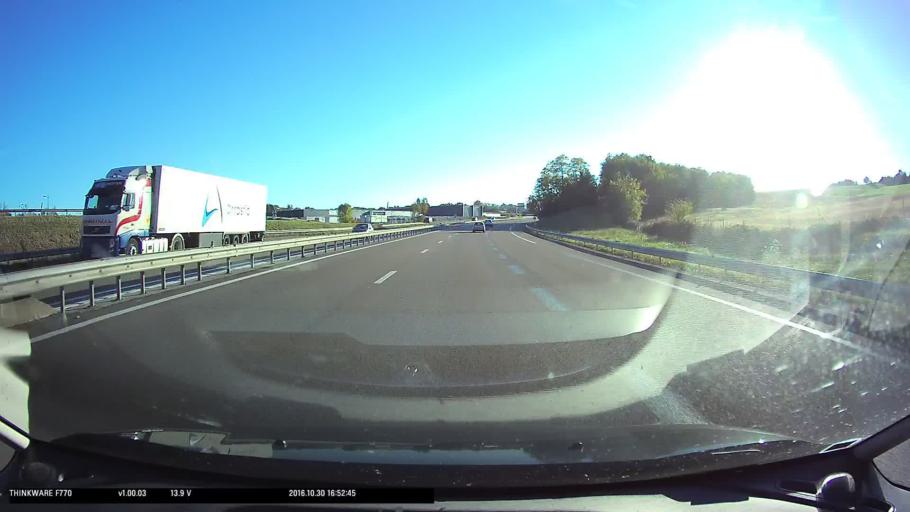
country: FR
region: Franche-Comte
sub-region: Departement du Doubs
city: Chemaudin
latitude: 47.2356
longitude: 5.8935
